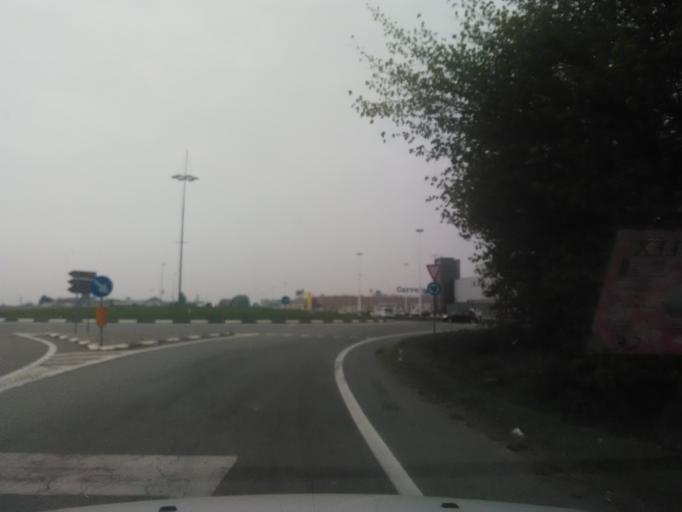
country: IT
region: Piedmont
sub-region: Provincia di Vercelli
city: Vercelli
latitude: 45.3164
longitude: 8.3948
